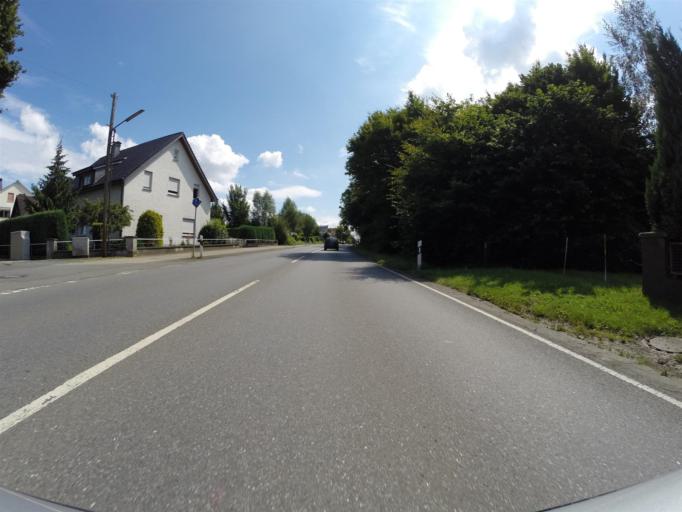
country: DE
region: North Rhine-Westphalia
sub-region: Regierungsbezirk Detmold
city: Hiddenhausen
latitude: 52.1518
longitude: 8.6465
